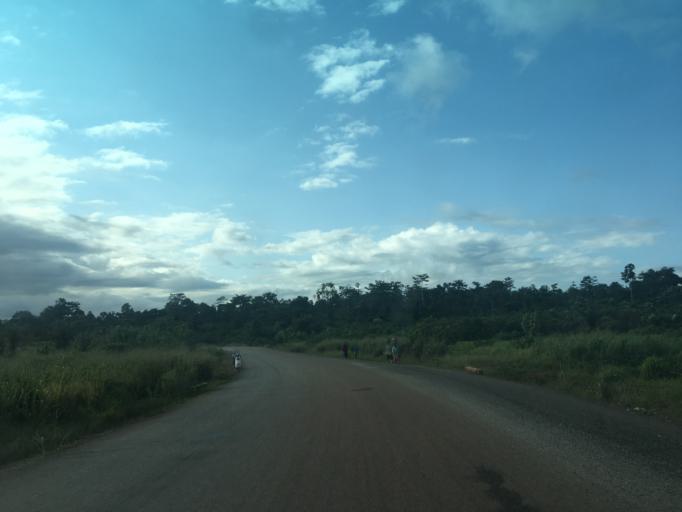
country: GH
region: Western
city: Bibiani
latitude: 6.1155
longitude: -2.3257
